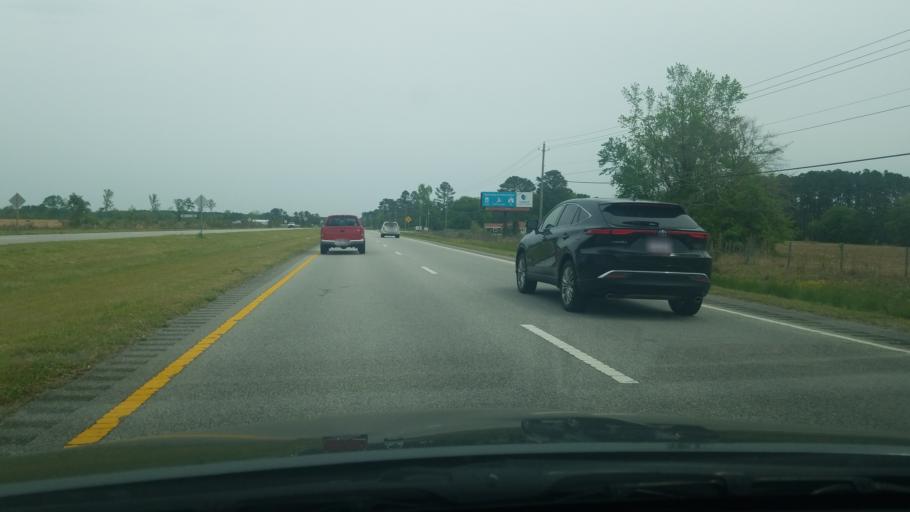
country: US
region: North Carolina
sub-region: Beaufort County
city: Washington
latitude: 35.4467
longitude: -77.1239
